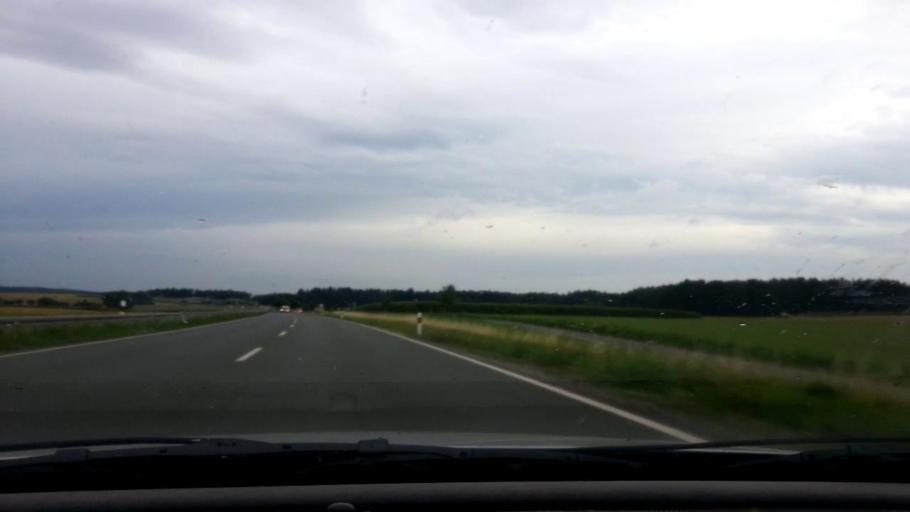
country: DE
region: Bavaria
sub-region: Upper Franconia
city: Speichersdorf
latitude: 49.8807
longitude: 11.7590
